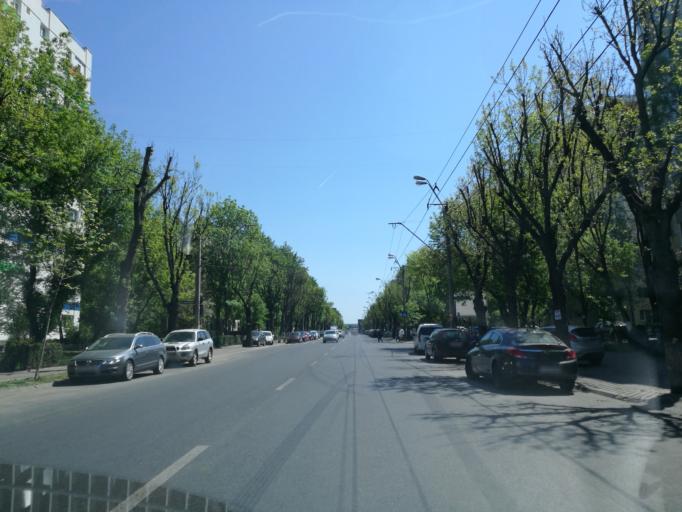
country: RO
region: Ilfov
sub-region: Comuna Popesti-Leordeni
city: Popesti-Leordeni
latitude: 44.3831
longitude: 26.1240
